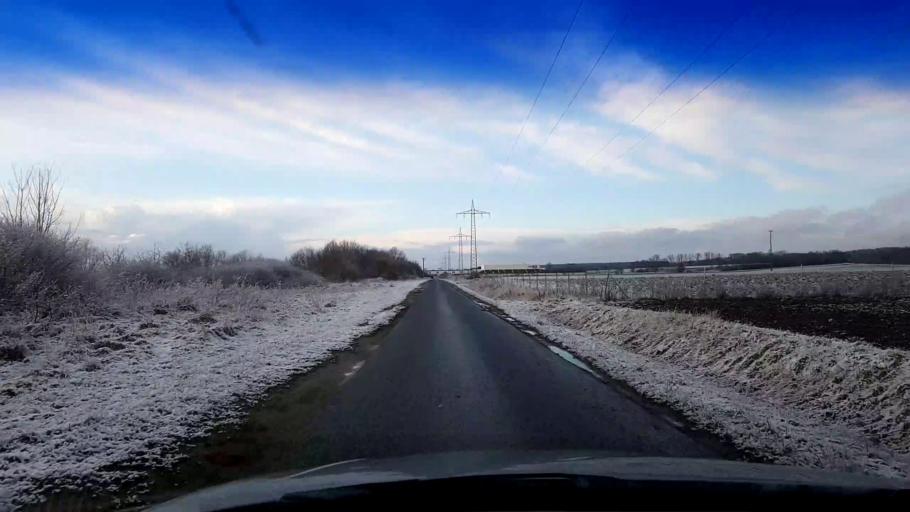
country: DE
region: Bavaria
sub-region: Upper Franconia
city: Altendorf
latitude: 49.8087
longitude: 11.0106
